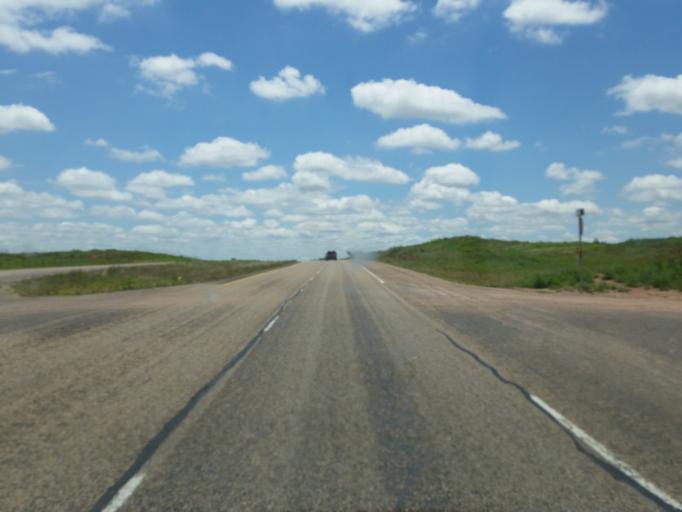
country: US
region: Texas
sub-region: Garza County
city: Post
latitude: 33.1104
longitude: -101.2704
